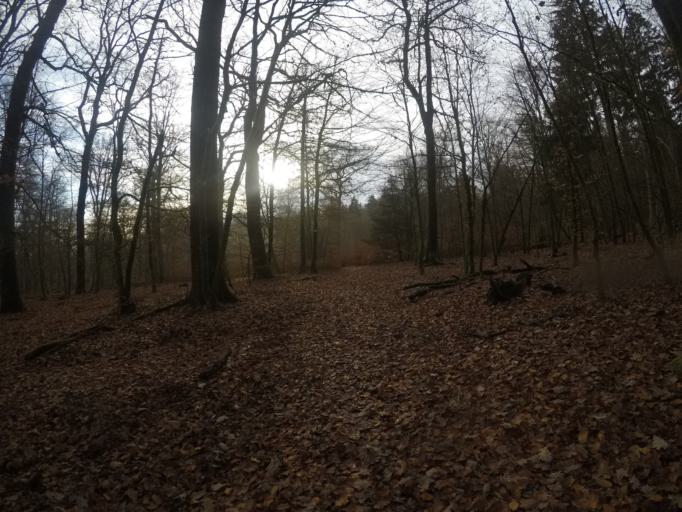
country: BE
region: Wallonia
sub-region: Province du Luxembourg
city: Habay-la-Vieille
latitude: 49.7595
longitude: 5.5989
